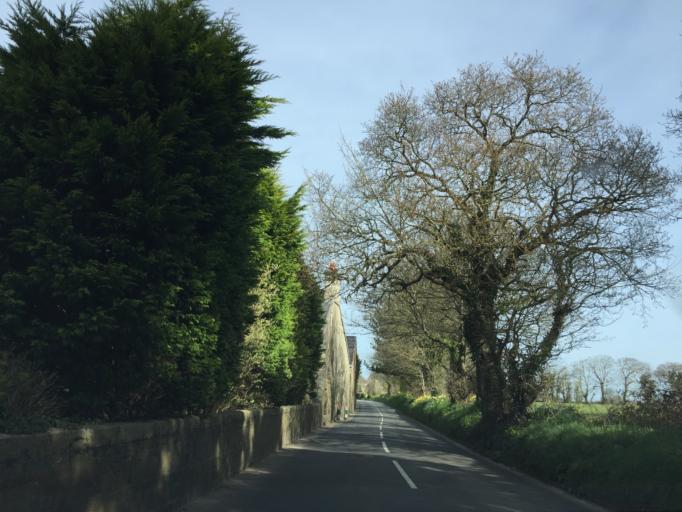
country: JE
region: St Helier
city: Saint Helier
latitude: 49.2204
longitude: -2.1411
